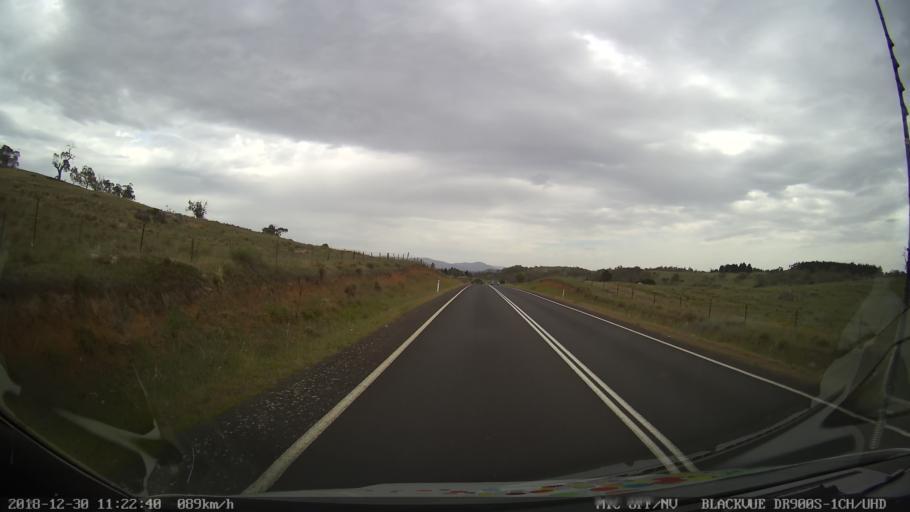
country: AU
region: New South Wales
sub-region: Snowy River
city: Jindabyne
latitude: -36.4970
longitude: 148.6707
